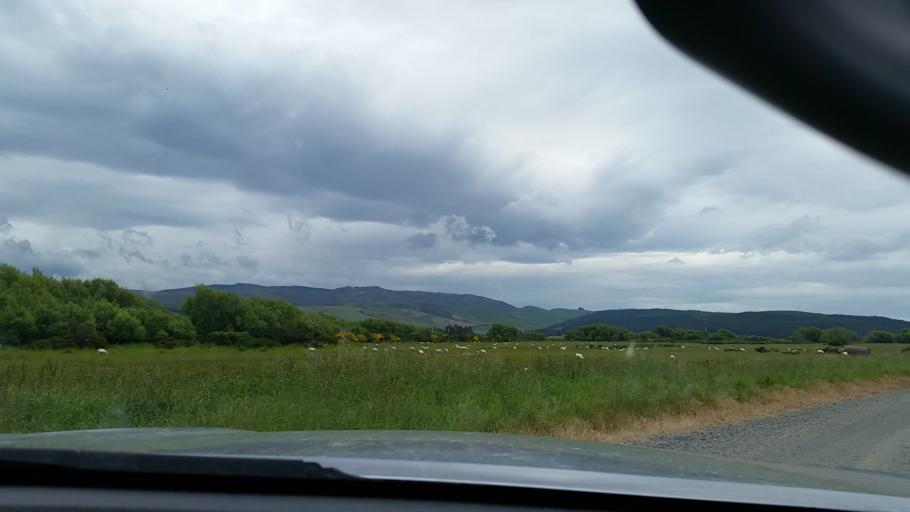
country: NZ
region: Southland
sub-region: Southland District
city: Winton
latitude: -45.8523
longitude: 168.1371
